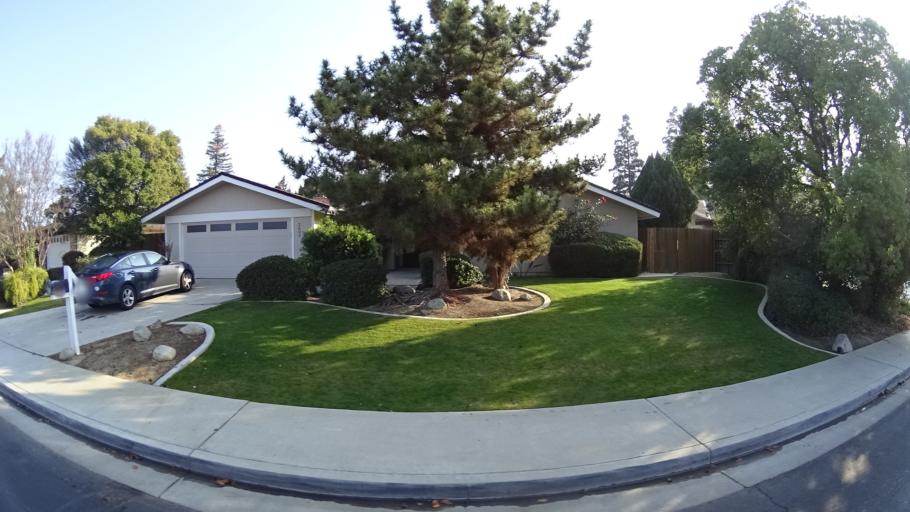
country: US
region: California
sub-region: Kern County
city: Greenacres
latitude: 35.3307
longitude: -119.0883
